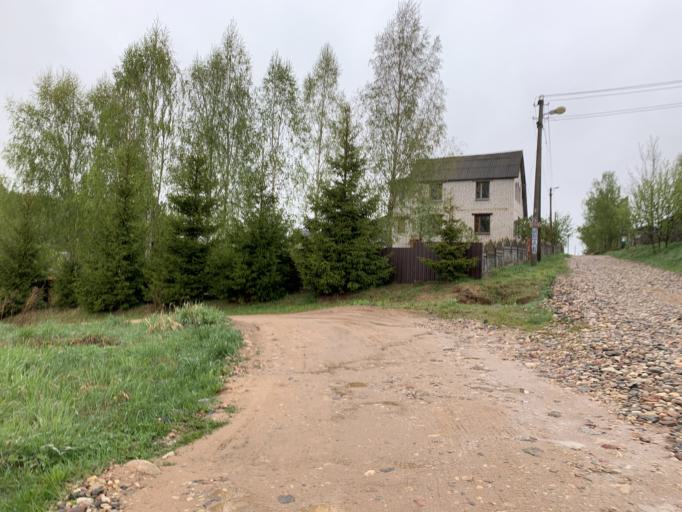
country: BY
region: Minsk
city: Lahoysk
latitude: 54.1224
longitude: 27.8998
